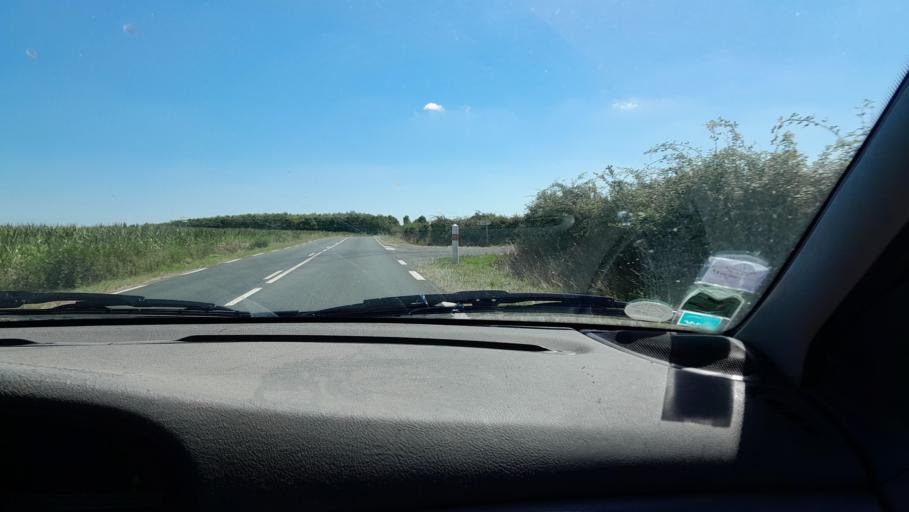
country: FR
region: Pays de la Loire
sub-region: Departement de la Loire-Atlantique
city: Saint-Mars-la-Jaille
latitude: 47.4840
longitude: -1.1740
